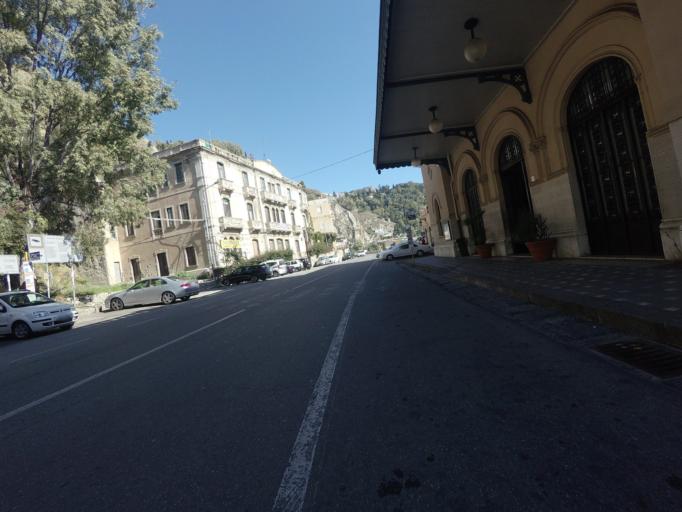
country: IT
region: Sicily
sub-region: Messina
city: Taormina
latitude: 37.8456
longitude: 15.2824
